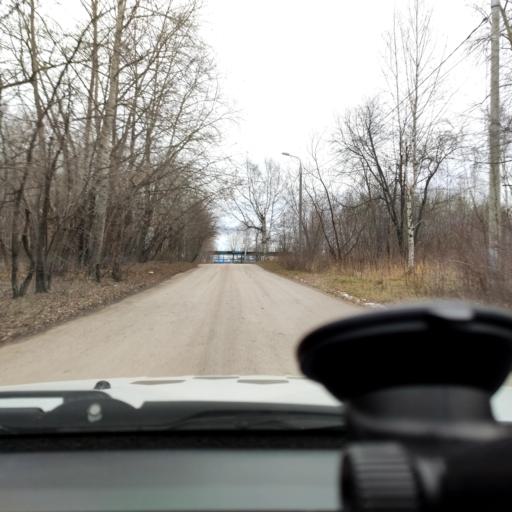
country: RU
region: Perm
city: Perm
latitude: 58.1183
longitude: 56.3736
